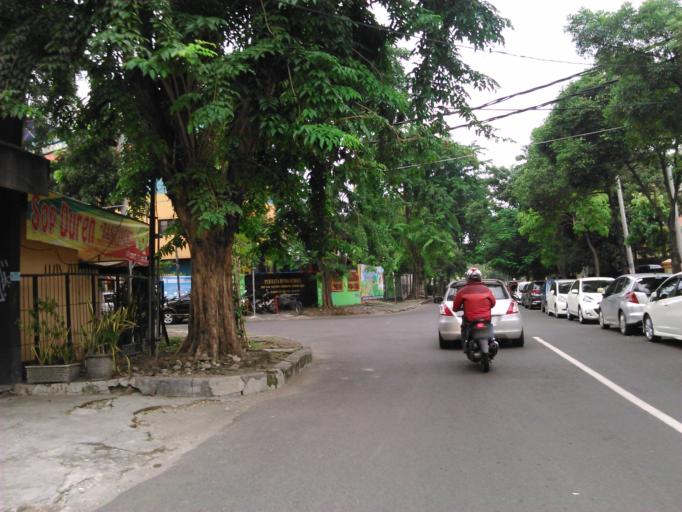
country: ID
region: East Java
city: Pacarkeling
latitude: -7.2581
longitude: 112.7504
